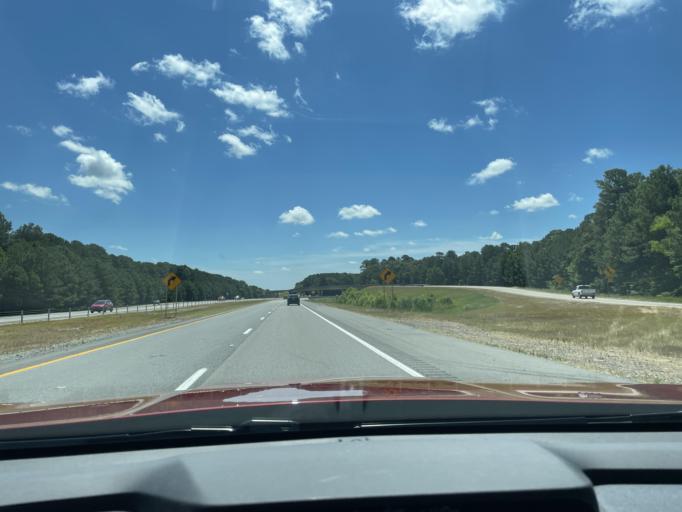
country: US
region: Arkansas
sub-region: Jefferson County
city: White Hall
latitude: 34.2460
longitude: -92.0963
